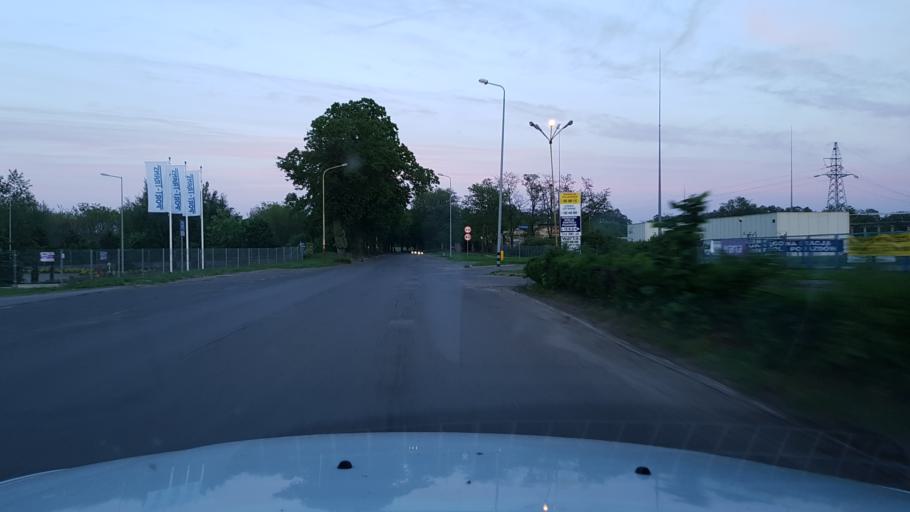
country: PL
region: West Pomeranian Voivodeship
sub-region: Powiat goleniowski
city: Goleniow
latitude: 53.5562
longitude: 14.8492
